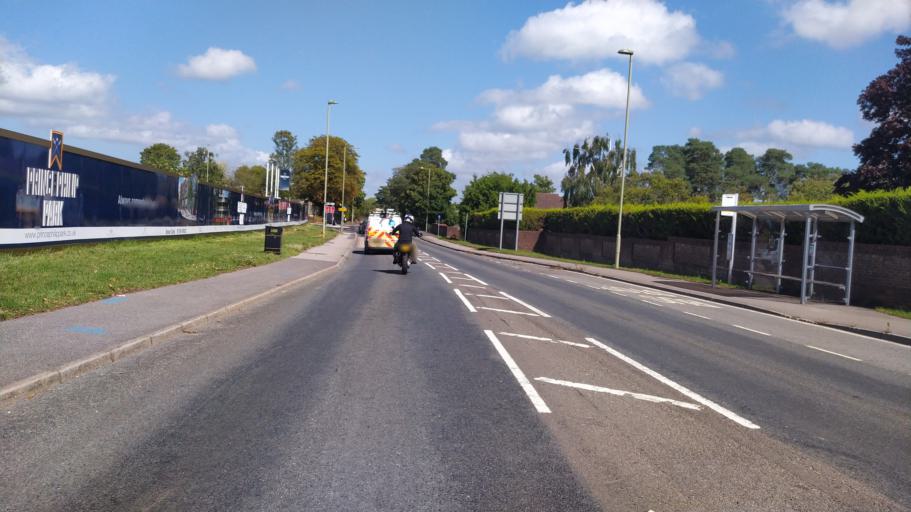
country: GB
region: England
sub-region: Hampshire
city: Bordon
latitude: 51.1128
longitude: -0.8629
